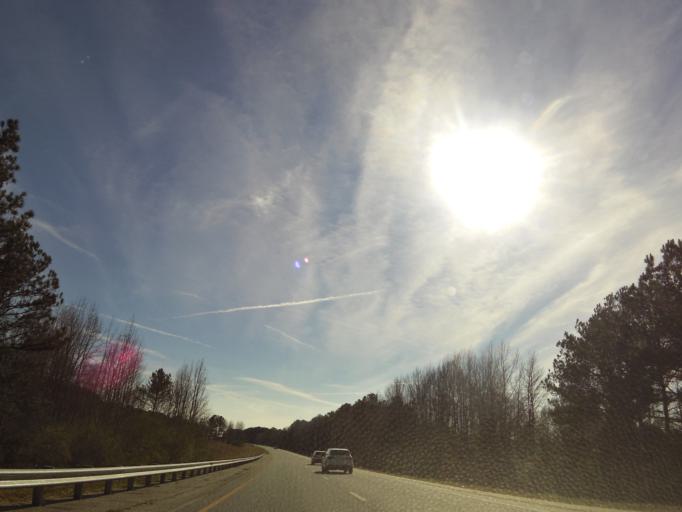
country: US
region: Georgia
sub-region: Troup County
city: La Grange
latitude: 32.9743
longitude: -84.9544
